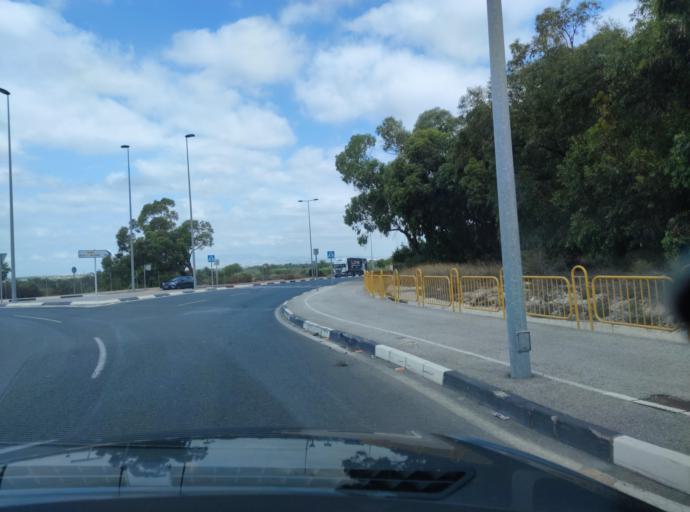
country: ES
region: Valencia
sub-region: Provincia de Alicante
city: Santa Pola
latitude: 38.2096
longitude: -0.5867
